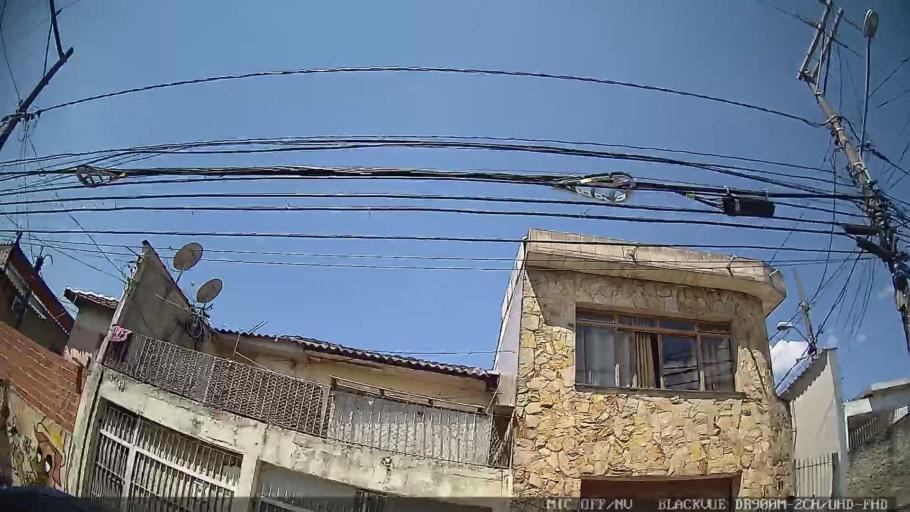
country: BR
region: Sao Paulo
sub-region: Guarulhos
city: Guarulhos
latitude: -23.5065
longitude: -46.5238
